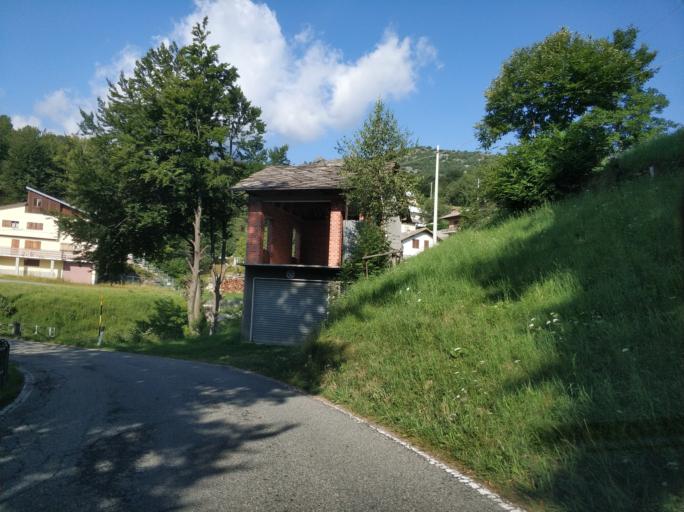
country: IT
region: Piedmont
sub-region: Provincia di Torino
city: Viu
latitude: 45.2070
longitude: 7.3783
